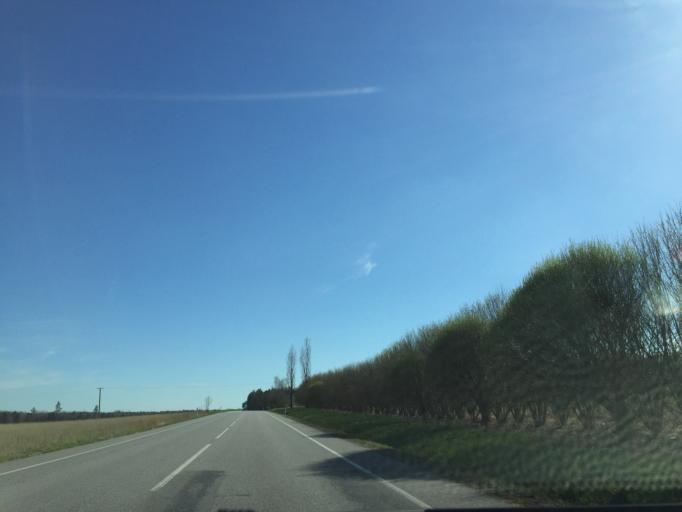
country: EE
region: Valgamaa
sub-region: Valga linn
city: Valga
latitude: 57.8780
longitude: 26.2792
